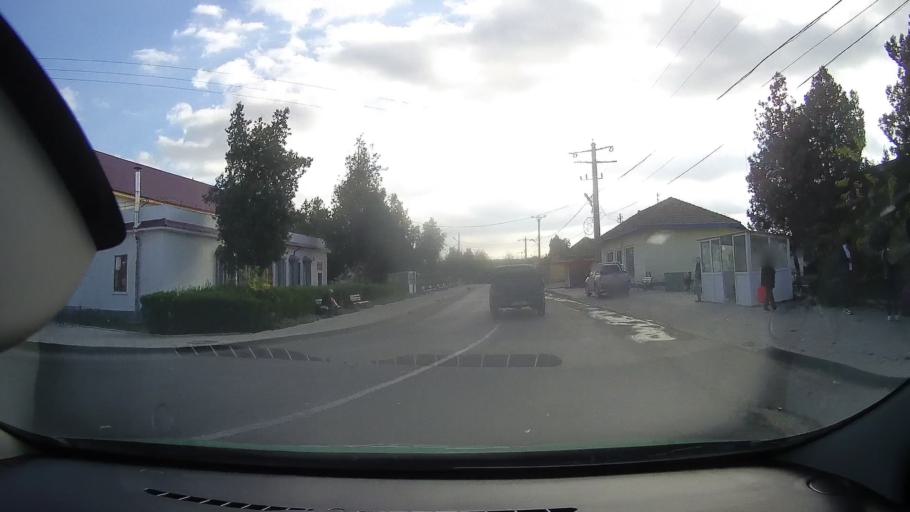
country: RO
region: Constanta
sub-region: Comuna Sacele
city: Sacele
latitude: 44.4872
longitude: 28.6444
